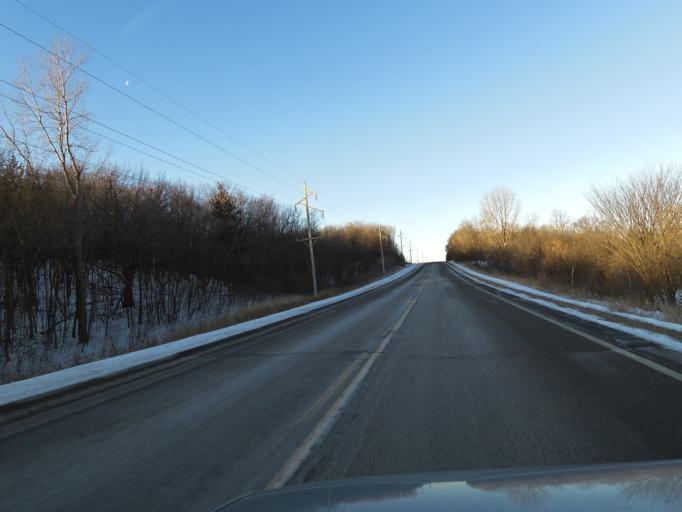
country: US
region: Minnesota
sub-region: Scott County
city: Prior Lake
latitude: 44.6745
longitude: -93.4257
